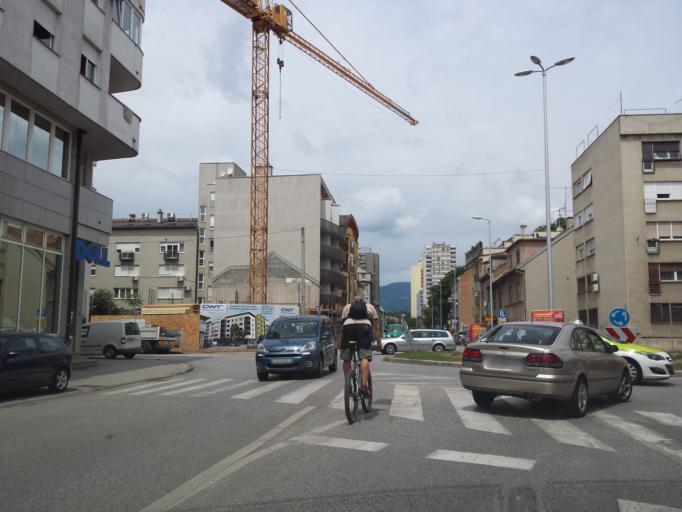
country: HR
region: Grad Zagreb
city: Zagreb - Centar
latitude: 45.8037
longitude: 15.9549
